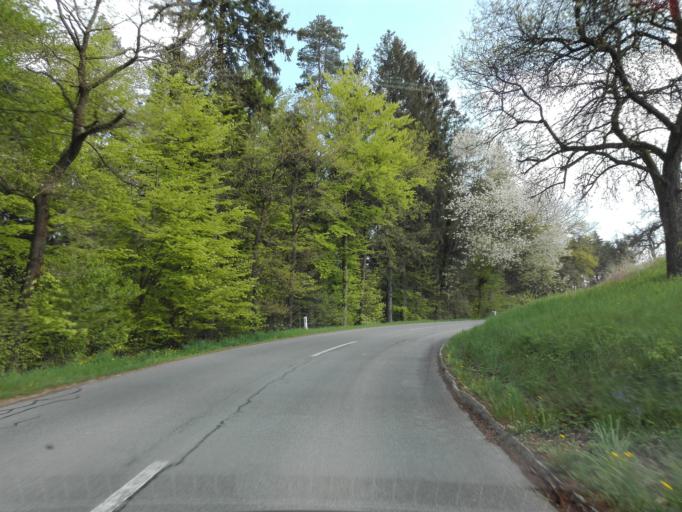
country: AT
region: Upper Austria
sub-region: Politischer Bezirk Perg
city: Perg
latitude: 48.2792
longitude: 14.6690
